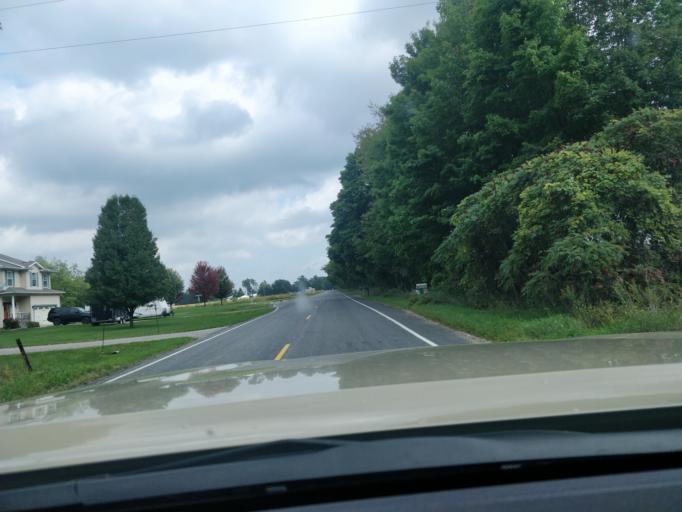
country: US
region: Michigan
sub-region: Kent County
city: Lowell
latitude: 42.8860
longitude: -85.3009
